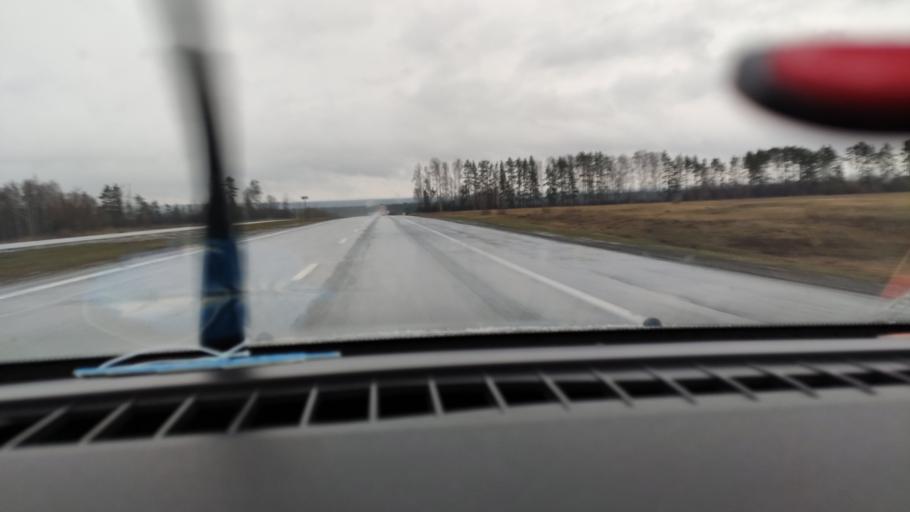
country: RU
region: Tatarstan
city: Yelabuga
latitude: 55.7846
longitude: 52.1705
